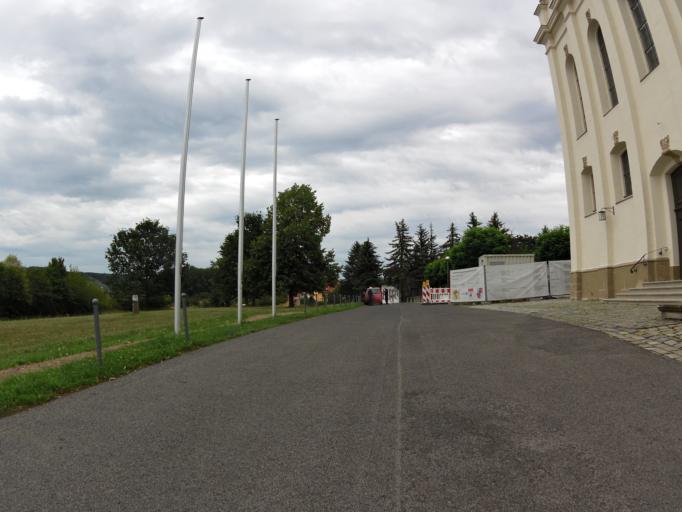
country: DE
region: Bavaria
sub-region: Regierungsbezirk Unterfranken
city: Sand
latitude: 49.9860
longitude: 10.6177
